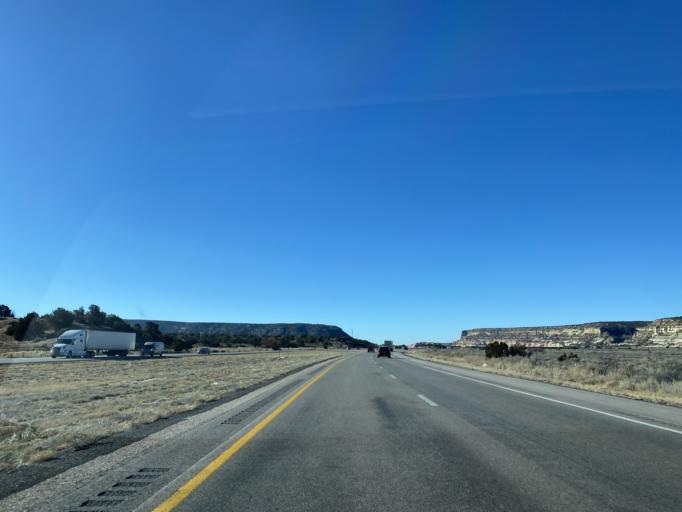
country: US
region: Arizona
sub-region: Apache County
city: Houck
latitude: 35.3853
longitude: -109.0137
